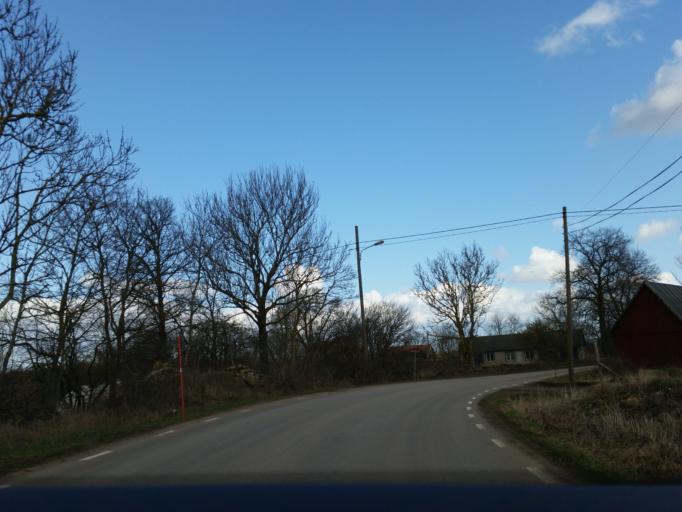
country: SE
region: Kalmar
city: Faerjestaden
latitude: 56.6860
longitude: 16.5480
